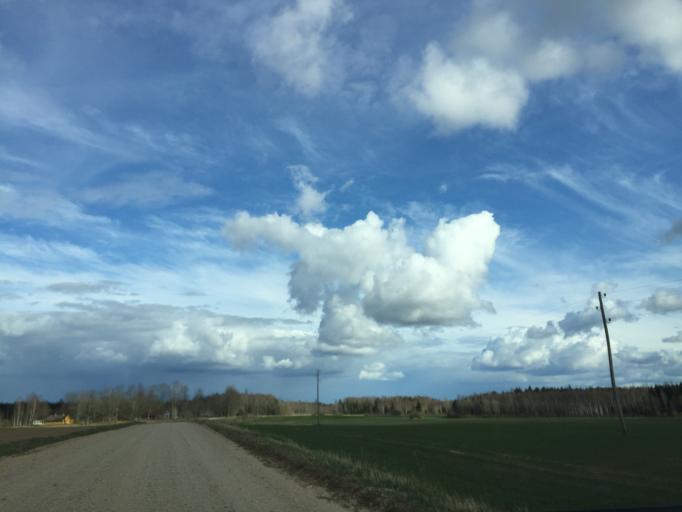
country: LV
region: Burtnieki
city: Matisi
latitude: 57.6116
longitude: 25.0265
